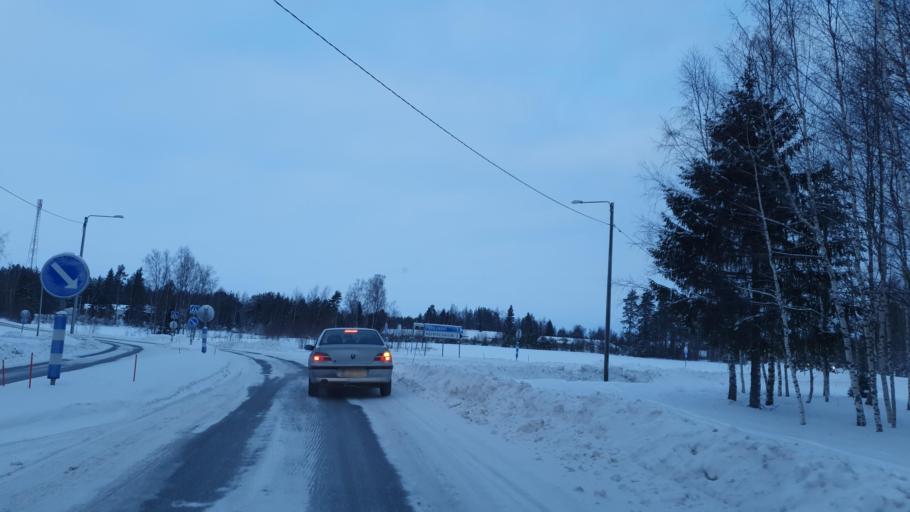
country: FI
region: Northern Ostrobothnia
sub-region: Oulu
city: Haukipudas
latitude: 65.2070
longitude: 25.3307
